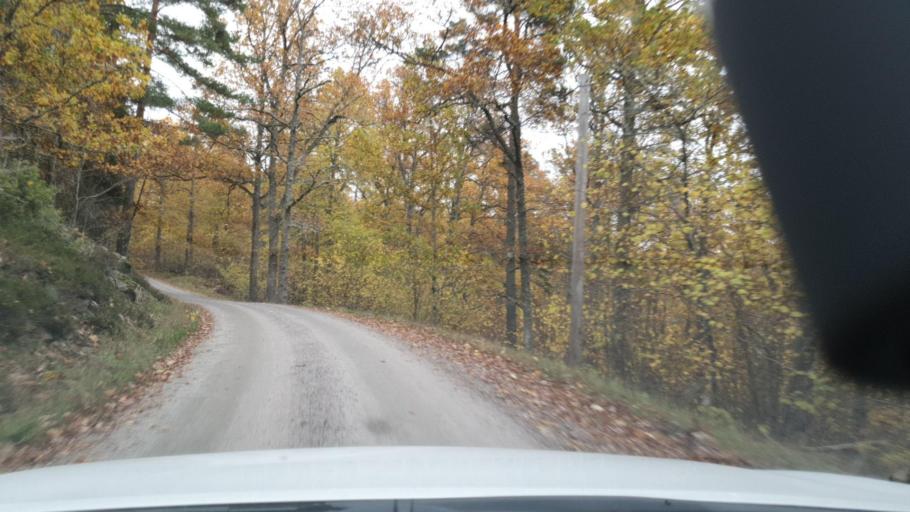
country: SE
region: Kalmar
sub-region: Vasterviks Kommun
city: Vaestervik
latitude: 57.7360
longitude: 16.4909
